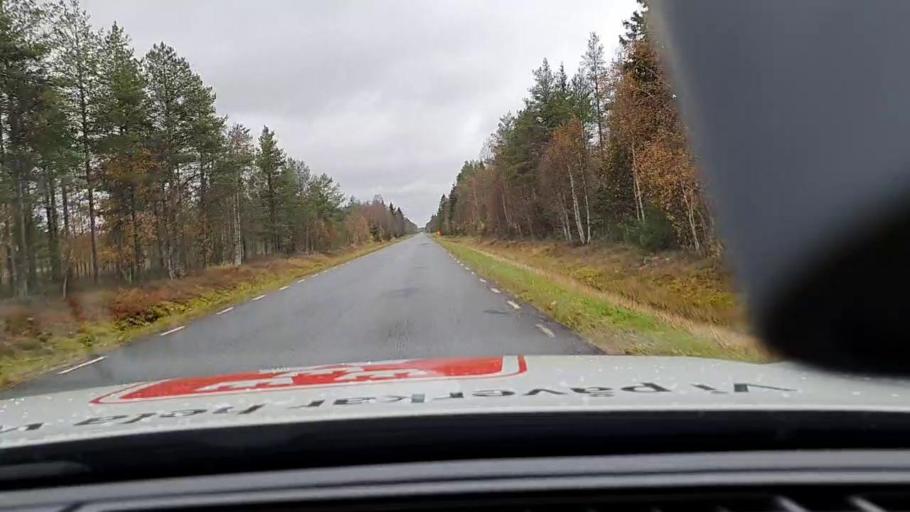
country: SE
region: Norrbotten
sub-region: Haparanda Kommun
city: Haparanda
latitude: 65.9115
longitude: 23.8290
